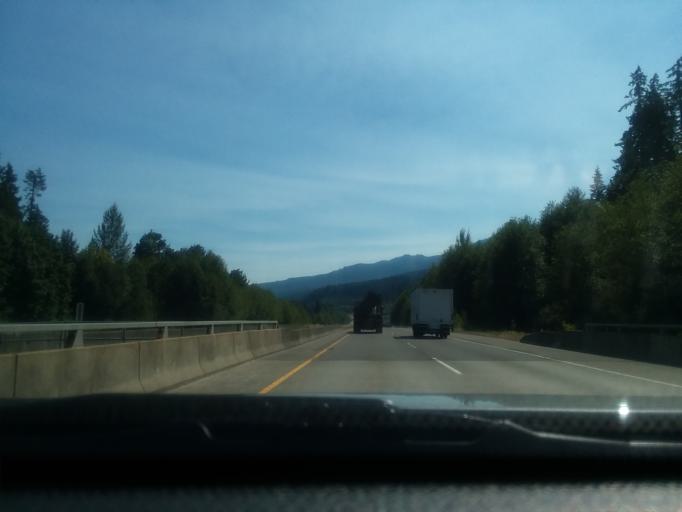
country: CA
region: British Columbia
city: Port Alberni
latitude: 49.4725
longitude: -124.8048
